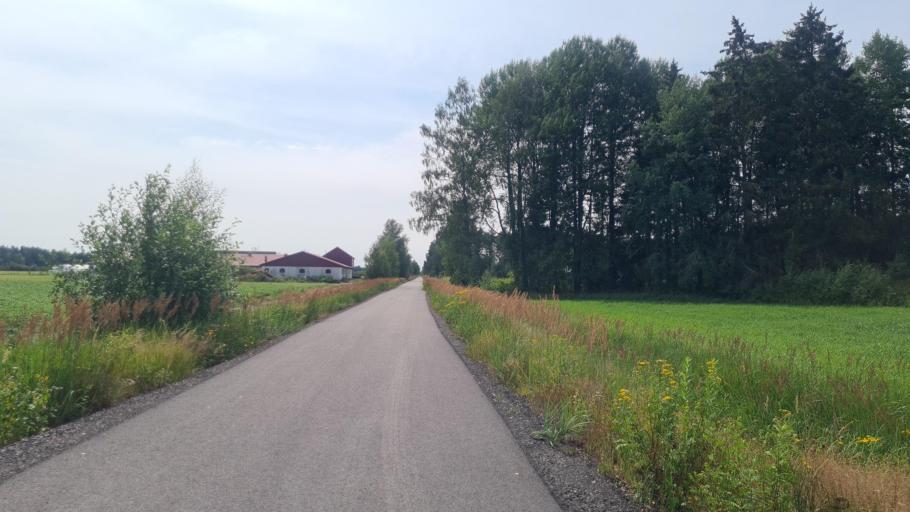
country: SE
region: Kronoberg
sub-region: Ljungby Kommun
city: Lagan
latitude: 56.9050
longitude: 13.9907
